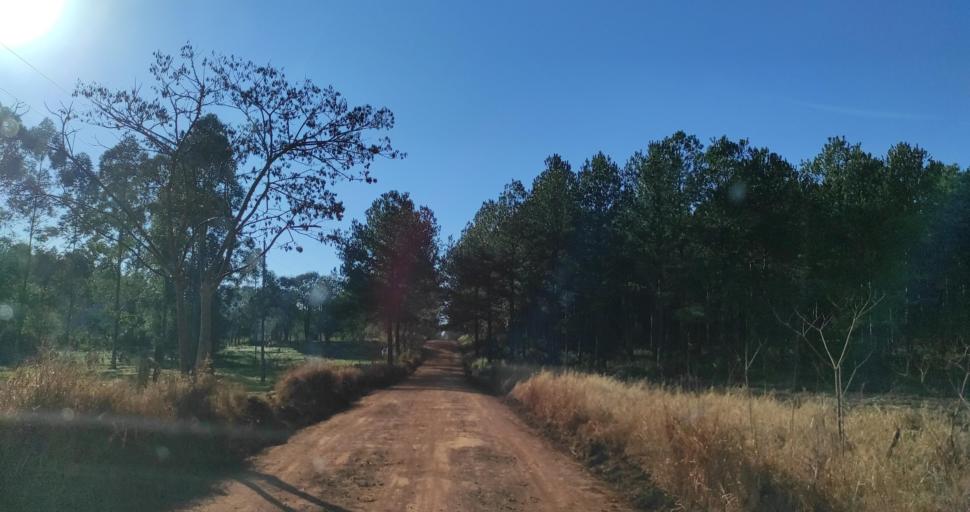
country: AR
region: Misiones
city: Capiovi
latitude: -26.8802
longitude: -55.0325
